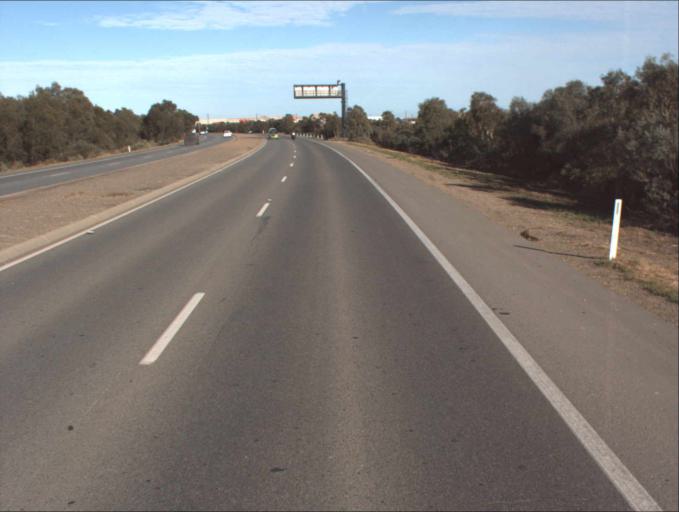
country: AU
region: South Australia
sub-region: Port Adelaide Enfield
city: Alberton
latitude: -34.8345
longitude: 138.5319
